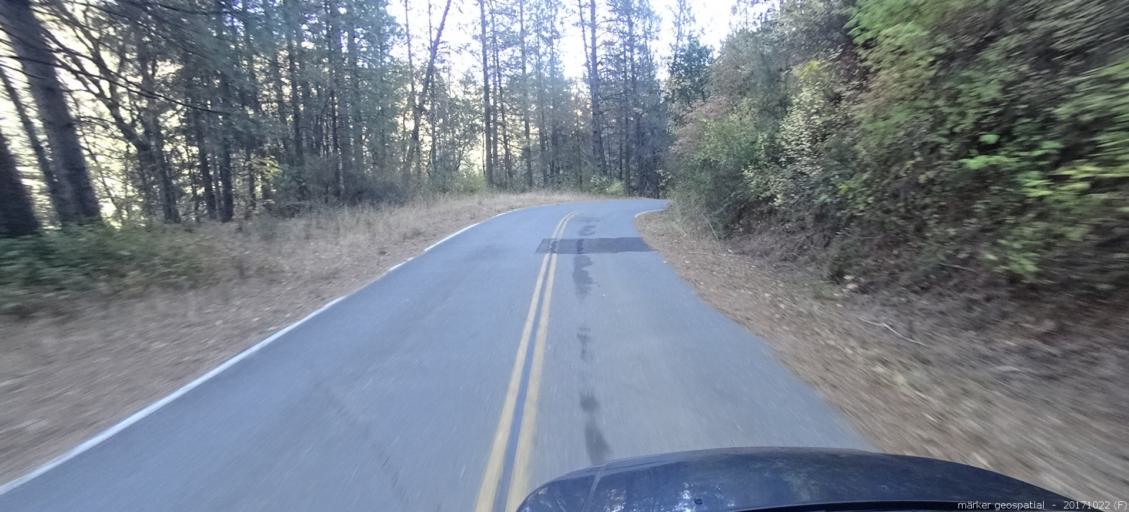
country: US
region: California
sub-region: Shasta County
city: Shasta Lake
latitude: 40.9115
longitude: -122.2394
